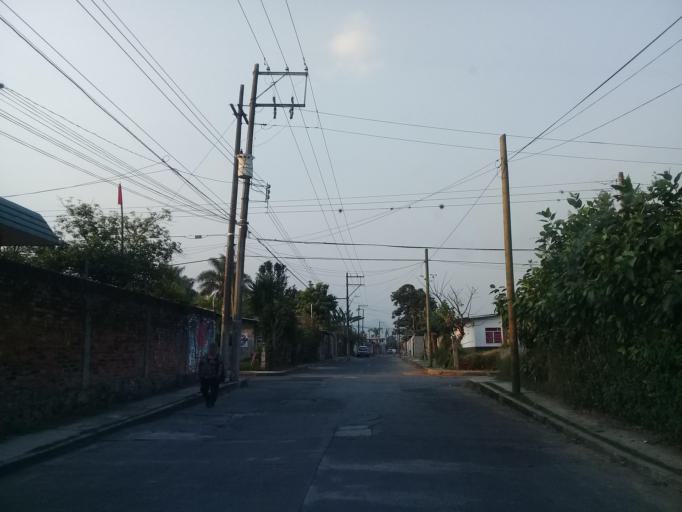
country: MX
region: Veracruz
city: Ixtac Zoquitlan
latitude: 18.8495
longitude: -97.0593
